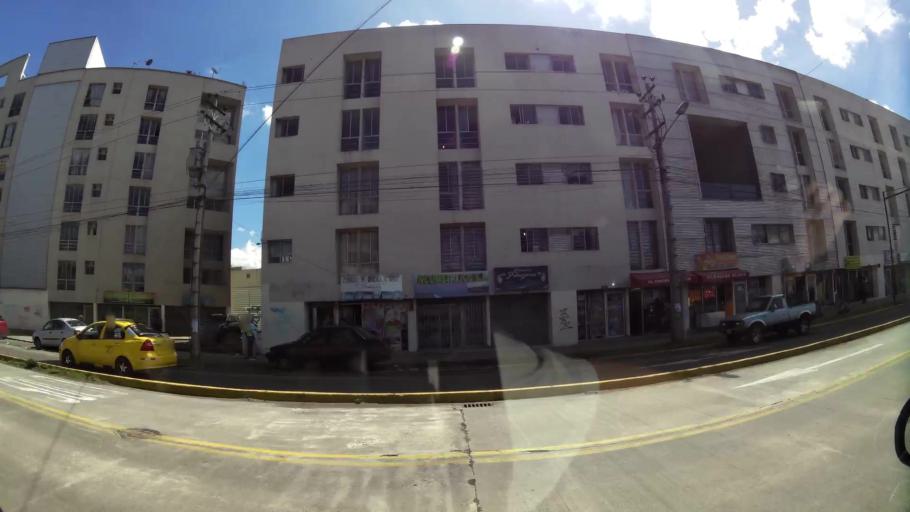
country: EC
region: Pichincha
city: Quito
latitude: -0.2978
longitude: -78.5492
